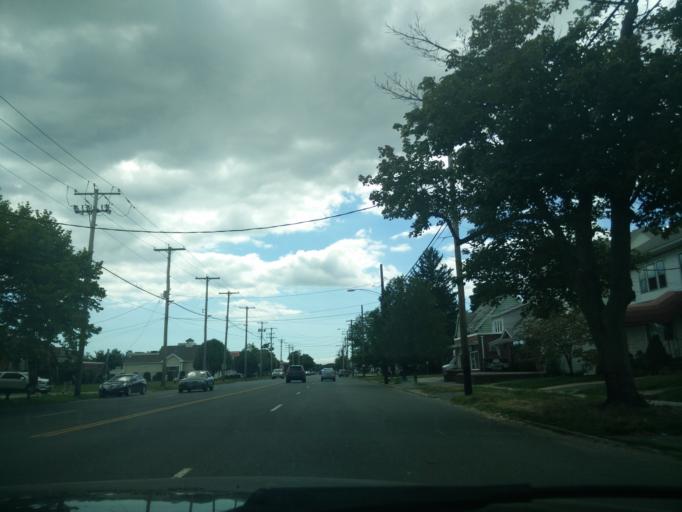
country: US
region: Connecticut
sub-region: New Haven County
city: New Haven
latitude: 41.3521
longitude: -72.9309
